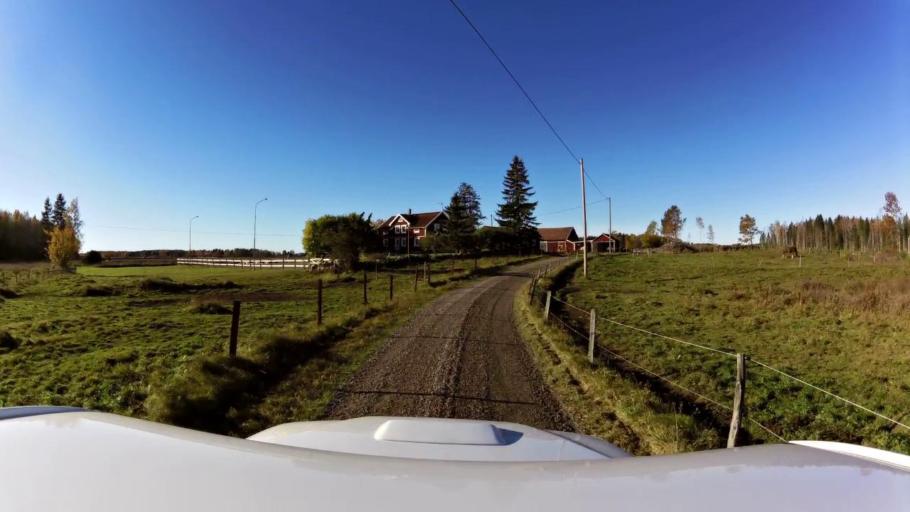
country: SE
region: OEstergoetland
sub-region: Linkopings Kommun
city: Ljungsbro
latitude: 58.5135
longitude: 15.4009
